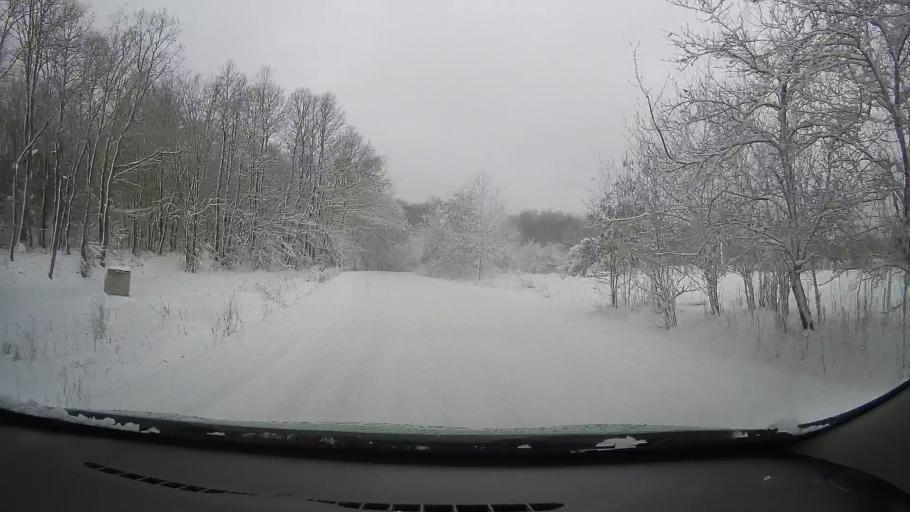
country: RO
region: Hunedoara
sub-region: Comuna Carjiti
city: Carjiti
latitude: 45.8427
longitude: 22.8540
